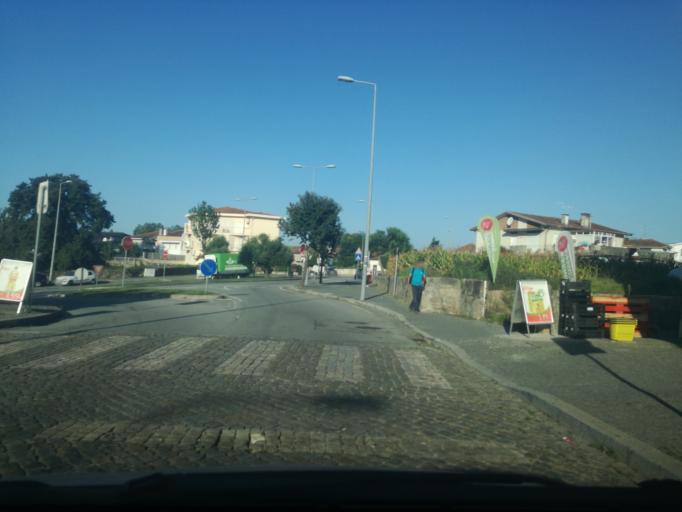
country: PT
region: Porto
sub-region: Maia
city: Milheiros
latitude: 41.2136
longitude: -8.5931
